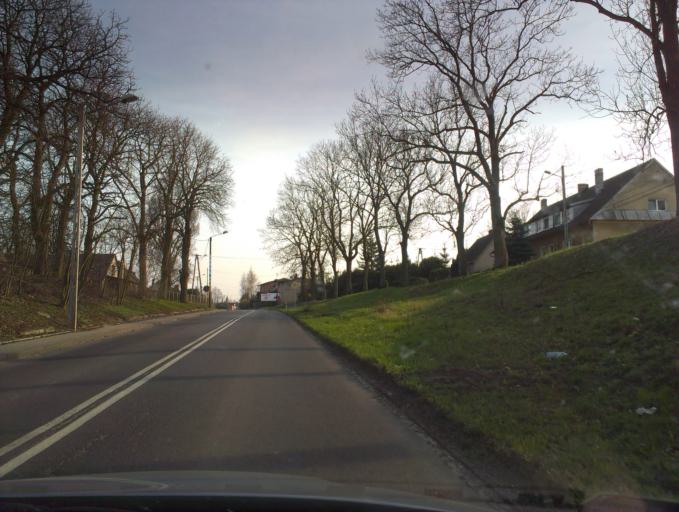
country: PL
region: Pomeranian Voivodeship
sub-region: Powiat czluchowski
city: Debrzno
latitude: 53.5303
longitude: 17.2307
